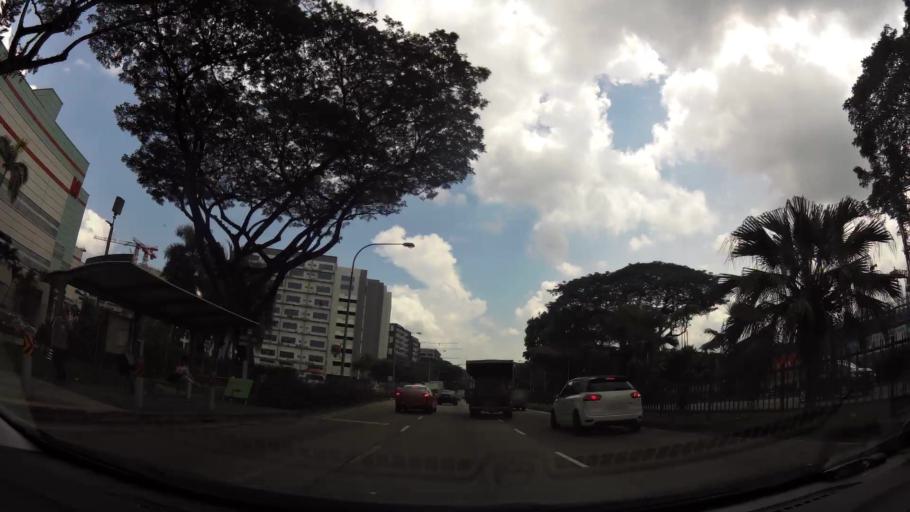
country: MY
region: Johor
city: Johor Bahru
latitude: 1.4447
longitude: 103.8105
